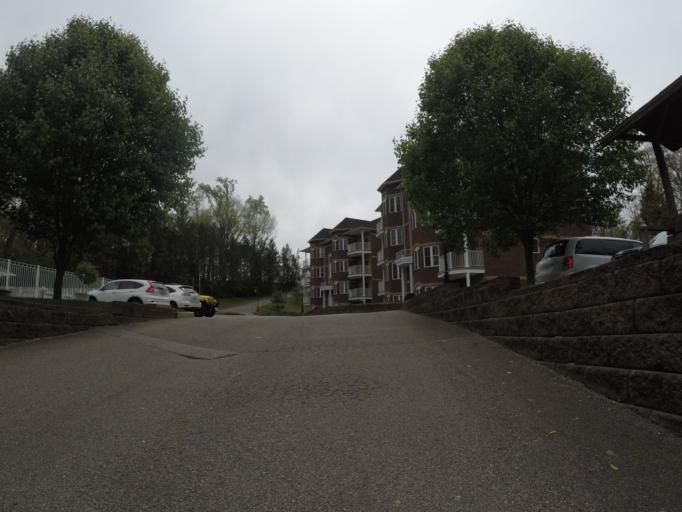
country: US
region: West Virginia
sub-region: Cabell County
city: Pea Ridge
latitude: 38.4104
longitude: -82.3452
